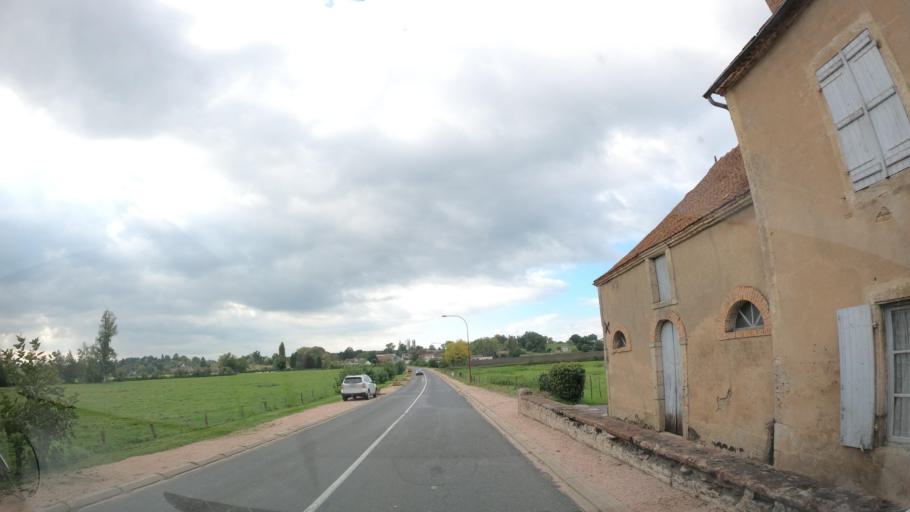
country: FR
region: Auvergne
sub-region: Departement de l'Allier
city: Lapalisse
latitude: 46.3802
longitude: 3.5902
